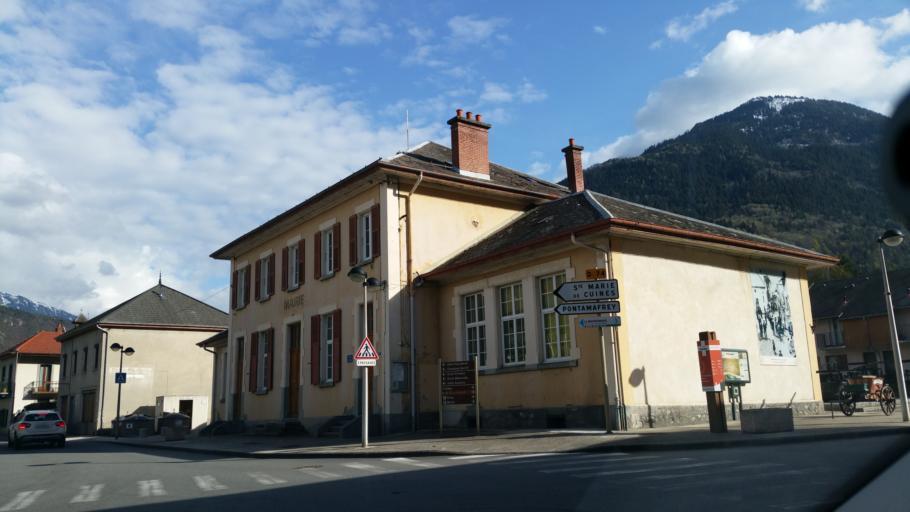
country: FR
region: Rhone-Alpes
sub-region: Departement de la Savoie
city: Saint-Etienne-de-Cuines
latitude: 45.3423
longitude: 6.2913
